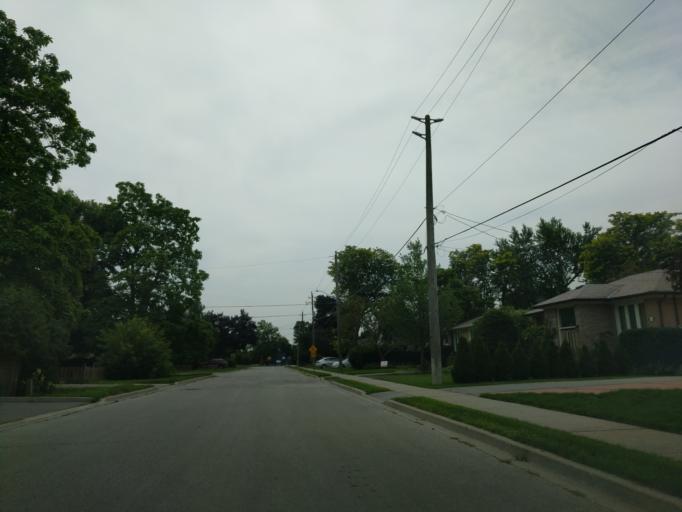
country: CA
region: Ontario
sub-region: York
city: Richmond Hill
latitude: 43.8712
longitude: -79.4190
